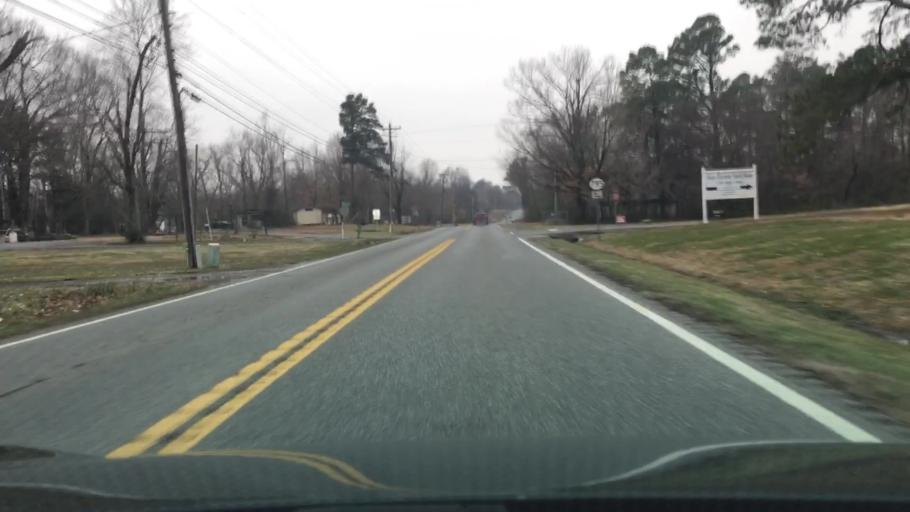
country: US
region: Kentucky
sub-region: Livingston County
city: Ledbetter
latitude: 36.9688
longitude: -88.4582
